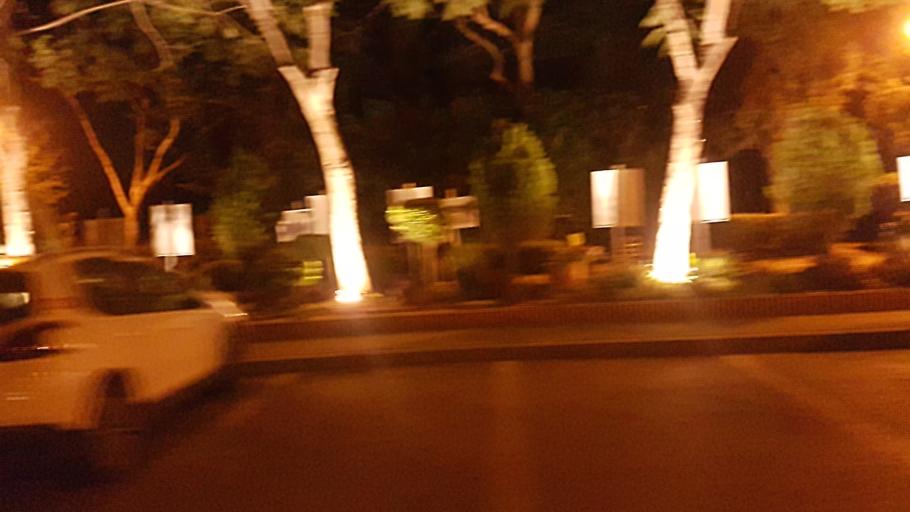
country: IL
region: Central District
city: Hod HaSharon
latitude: 32.1669
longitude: 34.8866
